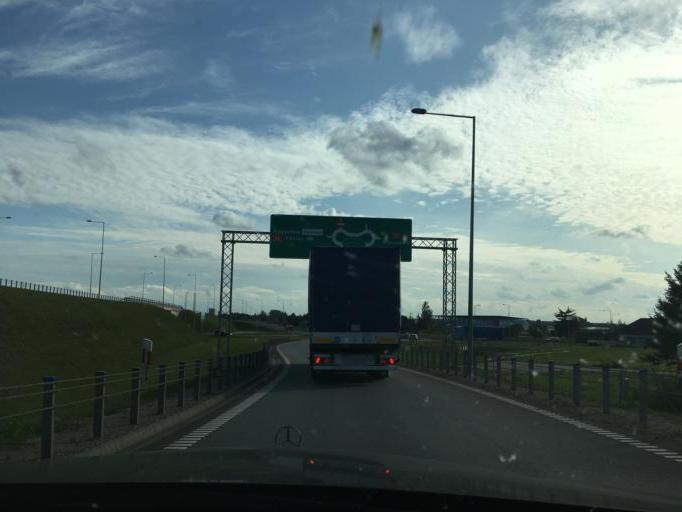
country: PL
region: Podlasie
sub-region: Powiat augustowski
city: Augustow
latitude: 53.8332
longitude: 22.9587
